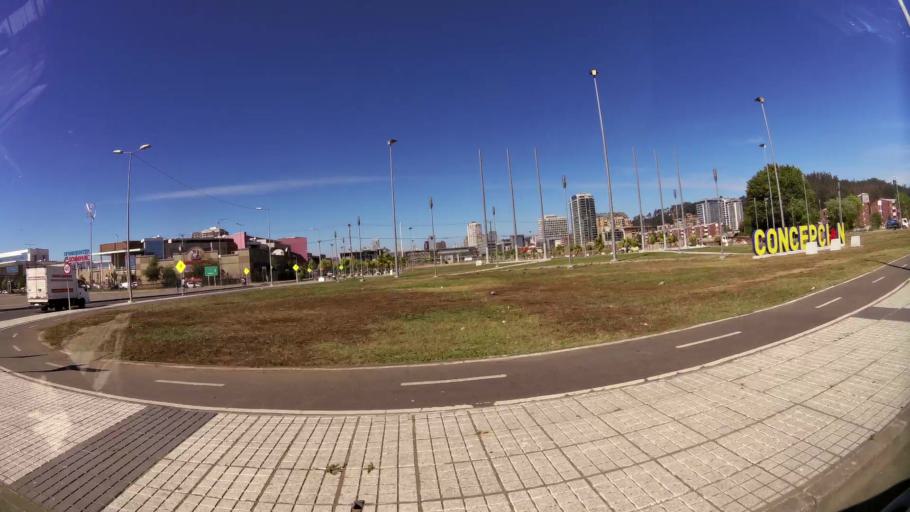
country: CL
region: Biobio
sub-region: Provincia de Concepcion
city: Concepcion
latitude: -36.8322
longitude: -73.0647
